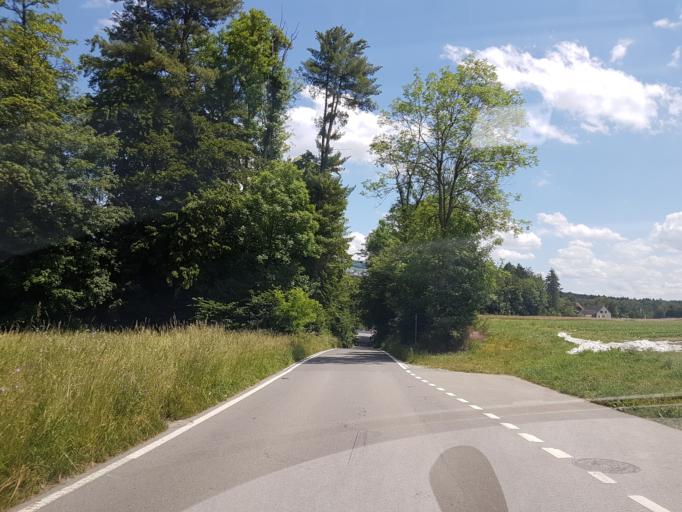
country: CH
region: Aargau
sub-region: Bezirk Baden
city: Niederrohrdorf
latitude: 47.3938
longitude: 8.2985
